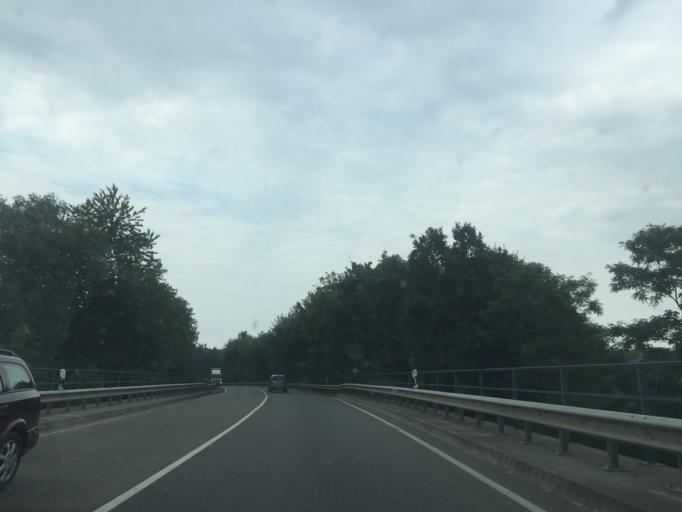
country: DE
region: Baden-Wuerttemberg
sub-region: Karlsruhe Region
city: Meckesheim
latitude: 49.3147
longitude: 8.8176
